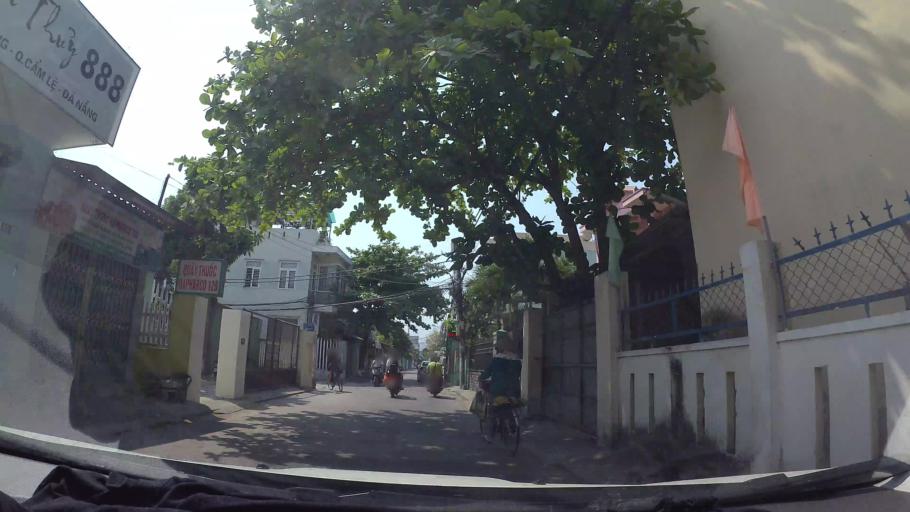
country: VN
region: Da Nang
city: Cam Le
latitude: 16.0143
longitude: 108.2033
